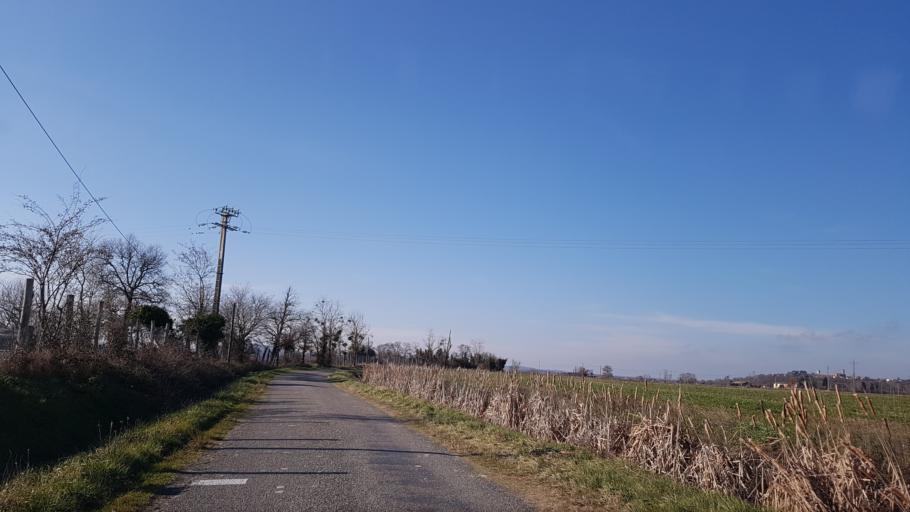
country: FR
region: Midi-Pyrenees
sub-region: Departement de l'Ariege
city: La Tour-du-Crieu
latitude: 43.1737
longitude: 1.6599
